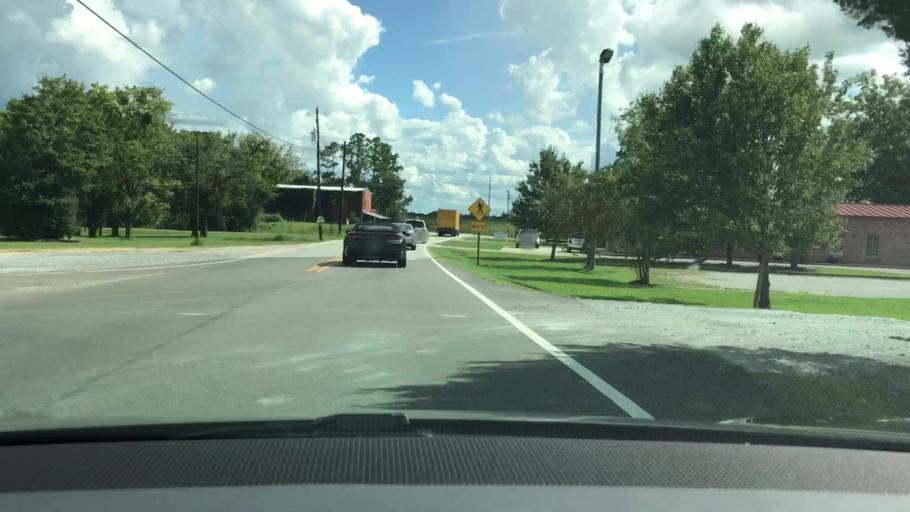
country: US
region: Alabama
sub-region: Montgomery County
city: Pike Road
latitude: 32.2833
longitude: -86.1025
